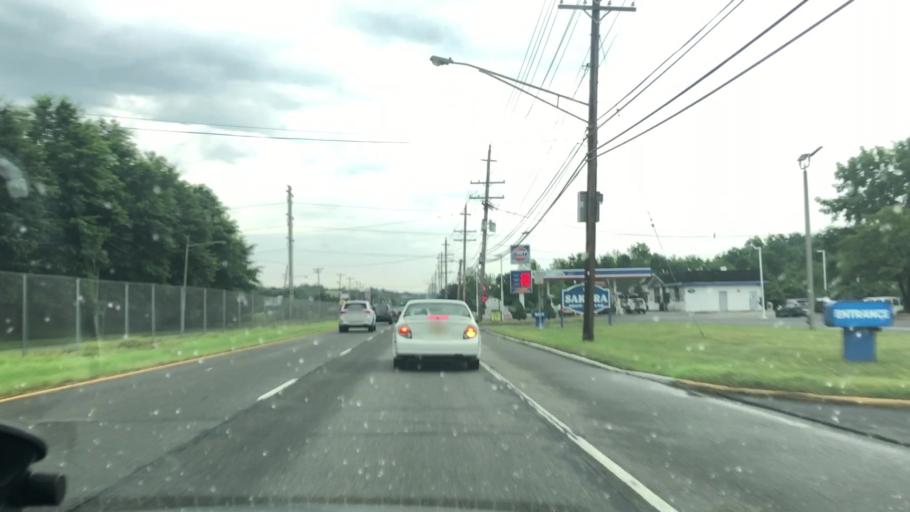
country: US
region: New Jersey
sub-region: Morris County
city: East Hanover
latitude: 40.8624
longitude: -74.3799
